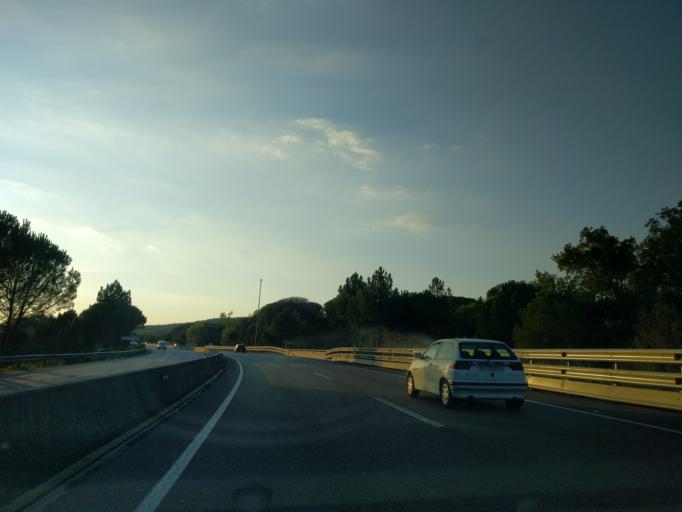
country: ES
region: Catalonia
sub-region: Provincia de Girona
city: Santa Cristina d'Aro
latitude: 41.8270
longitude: 2.9708
